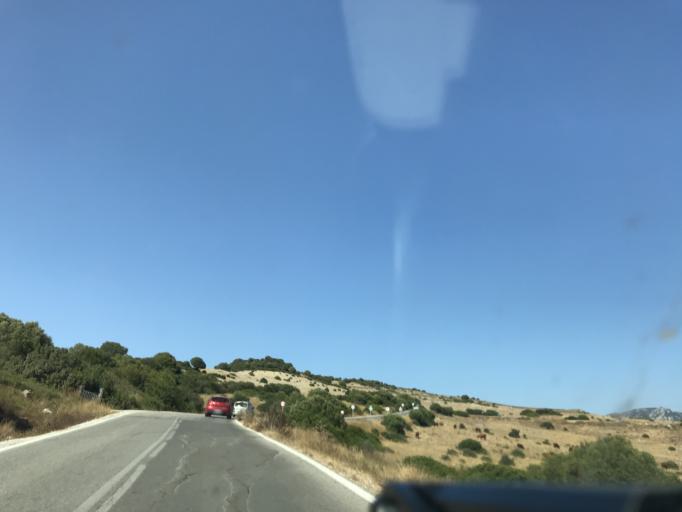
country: ES
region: Andalusia
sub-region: Provincia de Cadiz
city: Zahara de los Atunes
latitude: 36.1016
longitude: -5.7437
